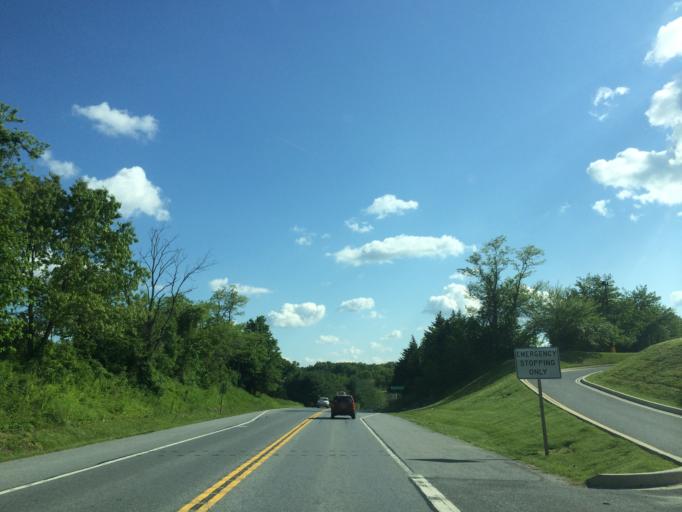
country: US
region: Maryland
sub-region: Baltimore County
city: Reisterstown
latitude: 39.4938
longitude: -76.8928
